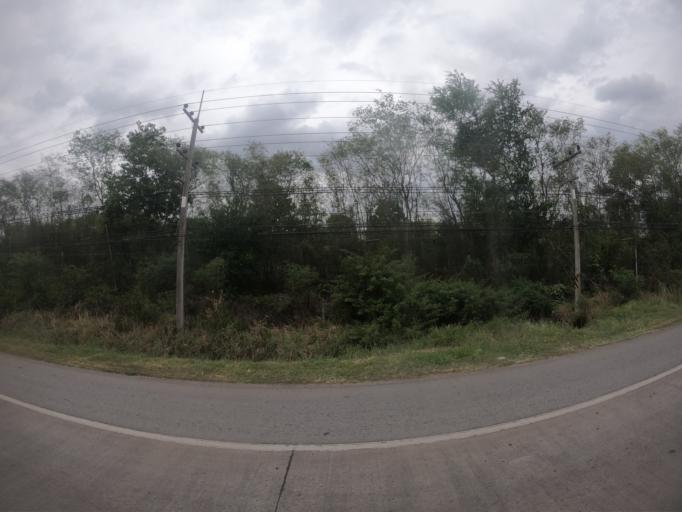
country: TH
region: Nakhon Ratchasima
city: Chok Chai
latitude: 14.7831
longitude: 102.1647
